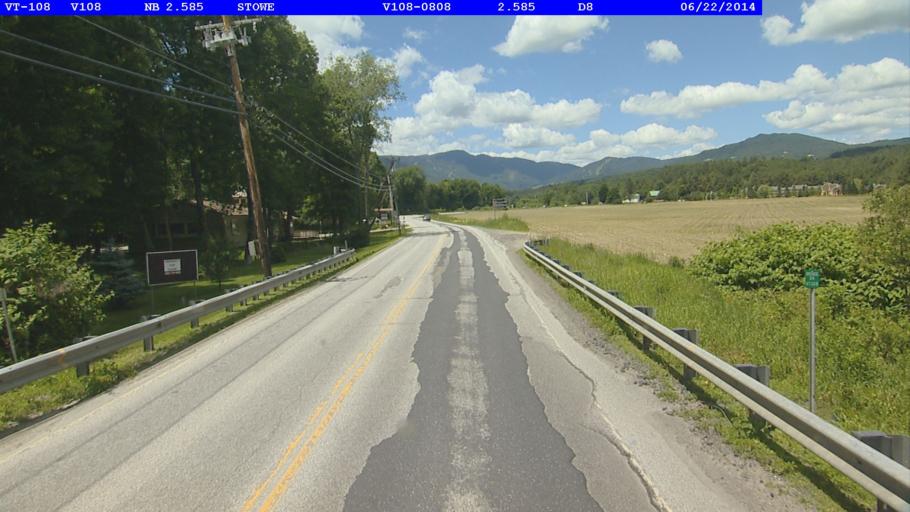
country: US
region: Vermont
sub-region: Lamoille County
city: Morristown
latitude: 44.4795
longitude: -72.7242
